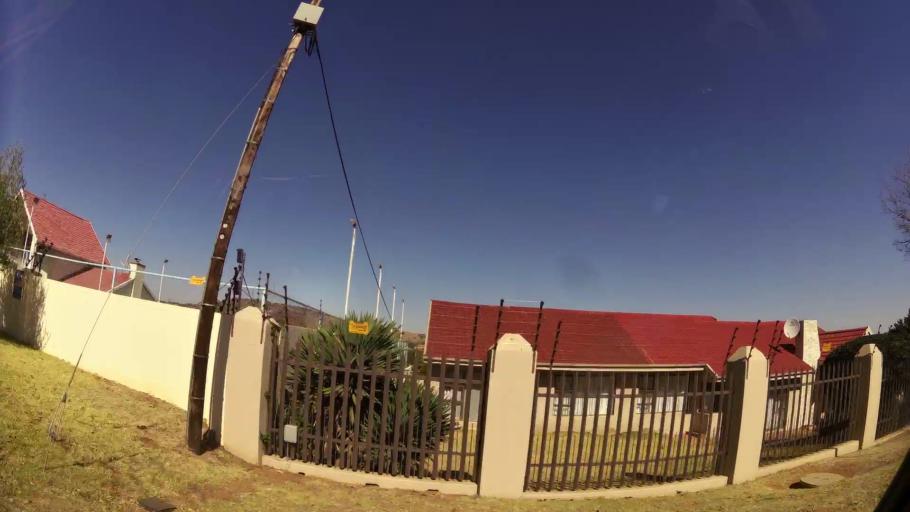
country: ZA
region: Gauteng
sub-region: City of Johannesburg Metropolitan Municipality
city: Johannesburg
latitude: -26.2717
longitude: 28.0184
